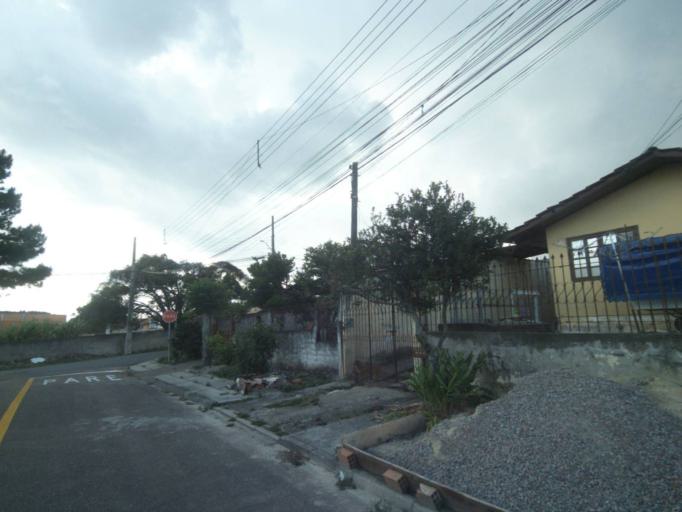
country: BR
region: Parana
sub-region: Sao Jose Dos Pinhais
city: Sao Jose dos Pinhais
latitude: -25.5293
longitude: -49.2735
